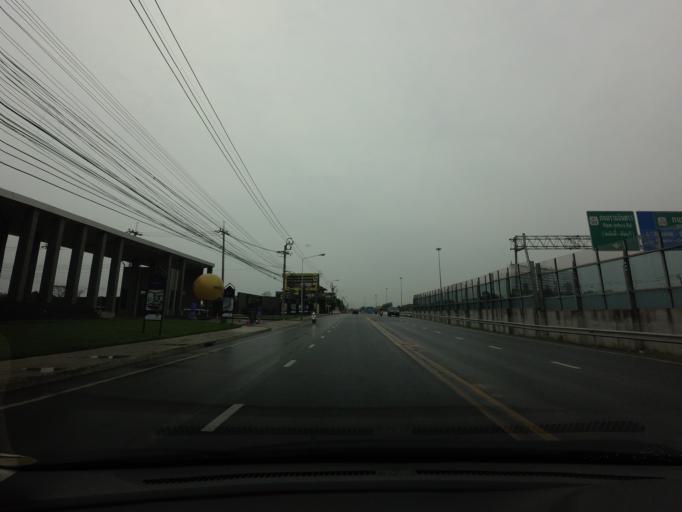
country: TH
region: Bangkok
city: Khan Na Yao
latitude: 13.8465
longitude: 100.6730
